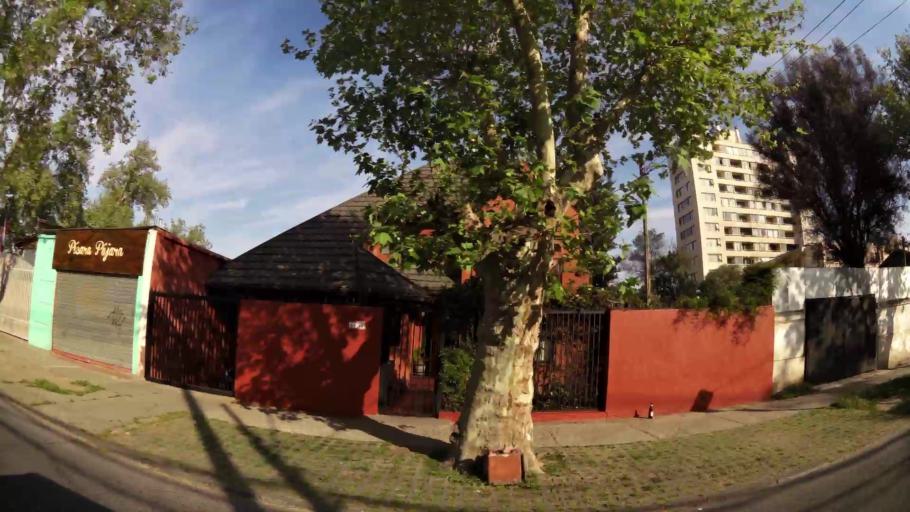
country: CL
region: Santiago Metropolitan
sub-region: Provincia de Santiago
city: Santiago
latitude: -33.5105
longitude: -70.6600
